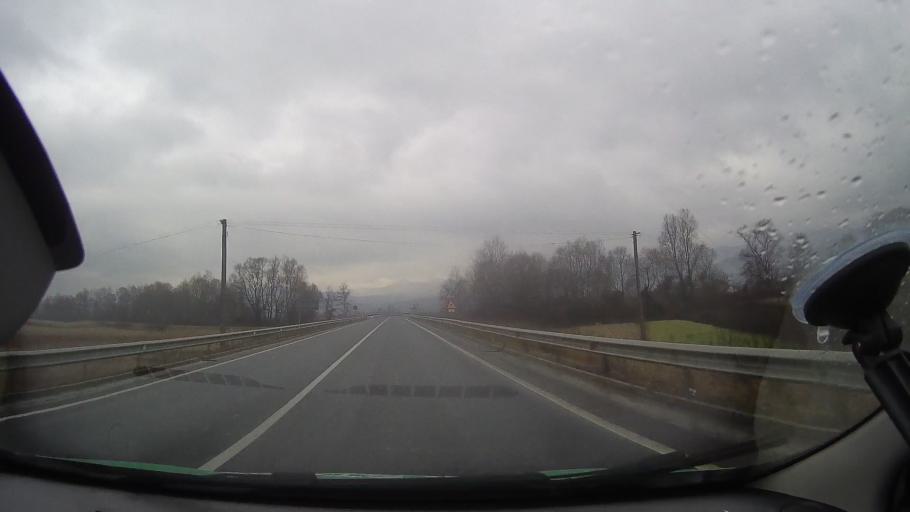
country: RO
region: Hunedoara
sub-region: Comuna Tomesti
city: Tomesti
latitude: 46.1830
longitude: 22.6590
